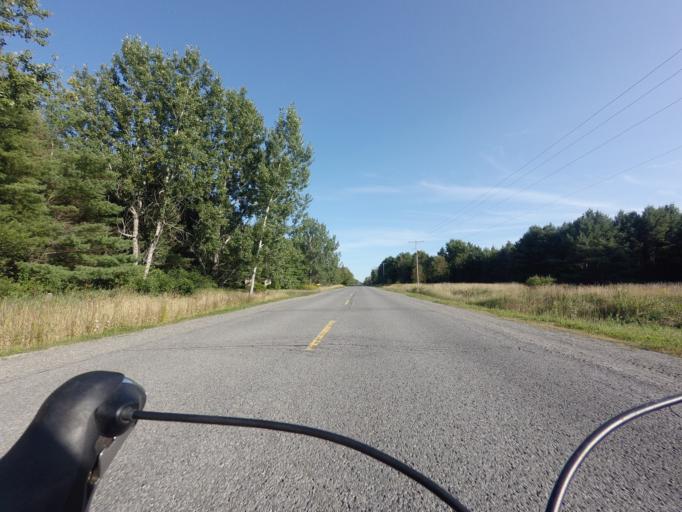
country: CA
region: Ontario
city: Bells Corners
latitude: 45.4524
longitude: -75.9883
